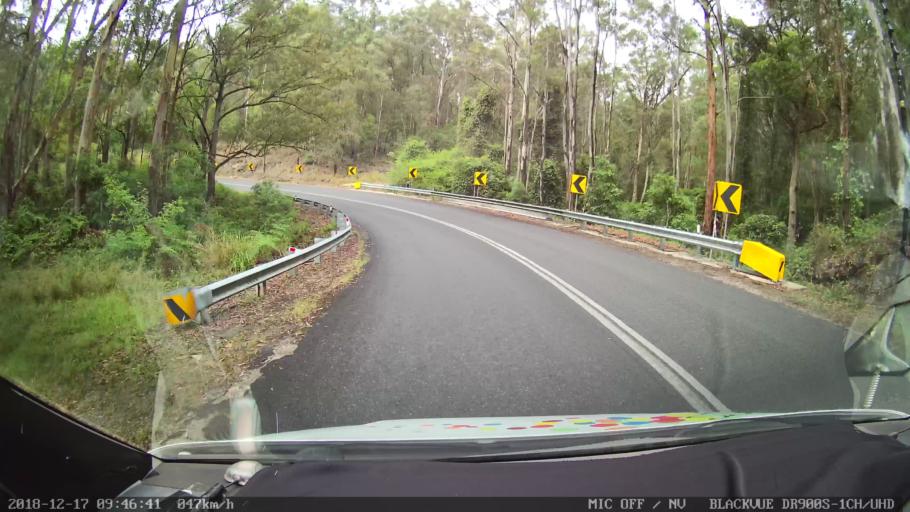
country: AU
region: New South Wales
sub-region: Tenterfield Municipality
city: Carrolls Creek
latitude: -28.9276
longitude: 152.3333
